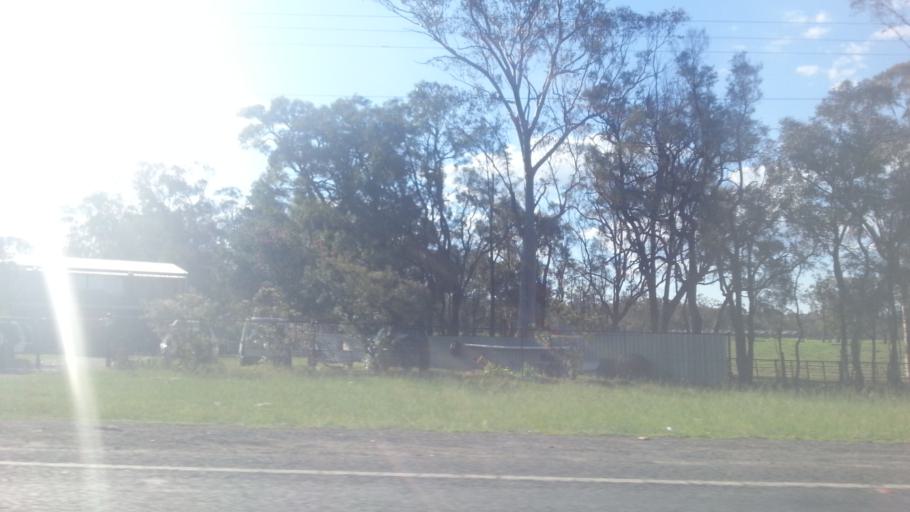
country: AU
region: New South Wales
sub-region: Penrith Municipality
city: Werrington Downs
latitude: -33.6775
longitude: 150.7450
